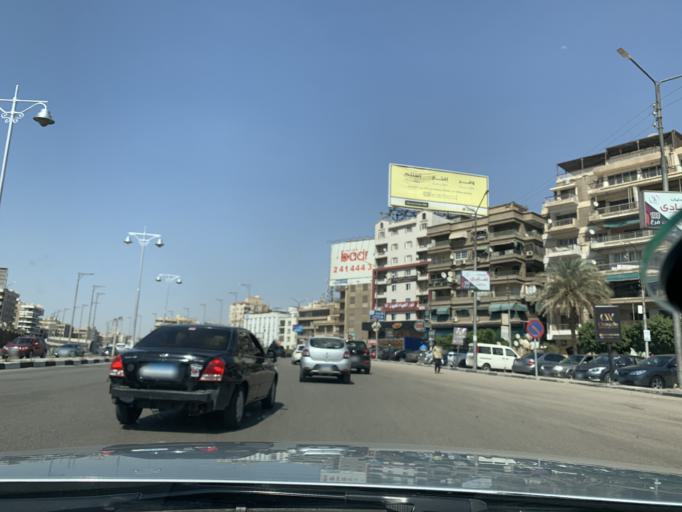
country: EG
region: Muhafazat al Qahirah
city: Cairo
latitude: 30.0850
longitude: 31.3324
